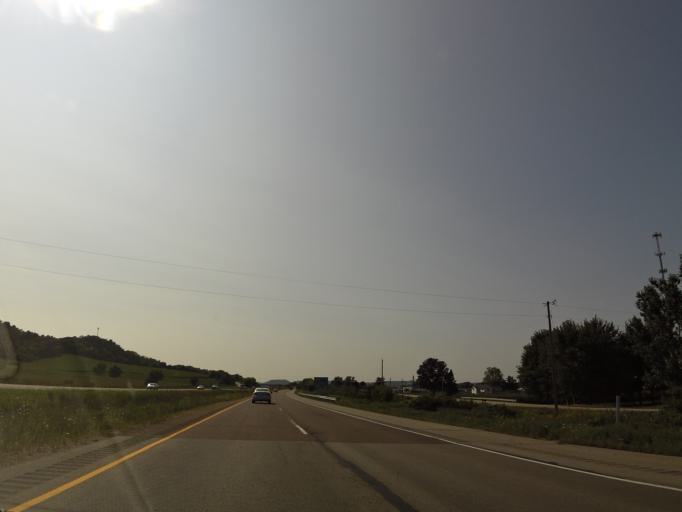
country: US
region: Wisconsin
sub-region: La Crosse County
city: West Salem
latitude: 43.8917
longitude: -91.0605
